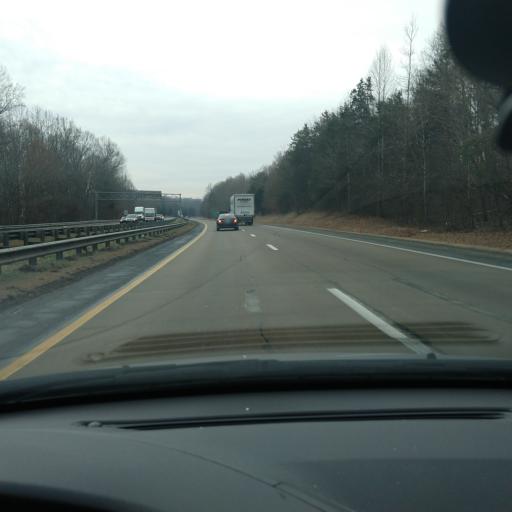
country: US
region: North Carolina
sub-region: Forsyth County
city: Winston-Salem
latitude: 36.0353
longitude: -80.2393
